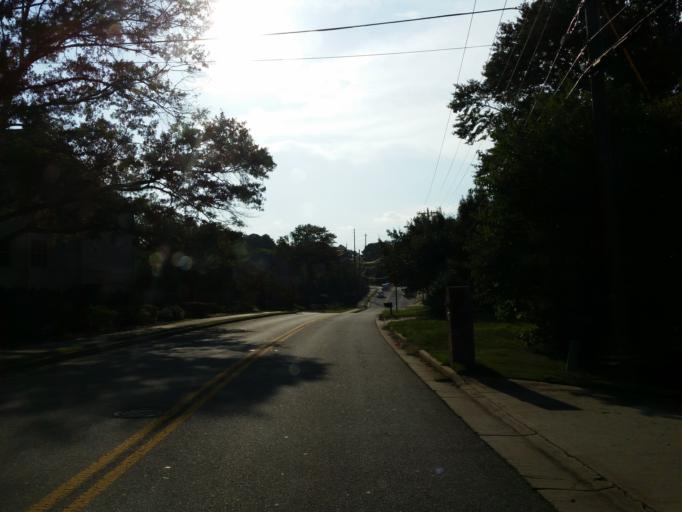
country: US
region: Georgia
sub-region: Cobb County
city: Marietta
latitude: 33.9674
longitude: -84.4605
